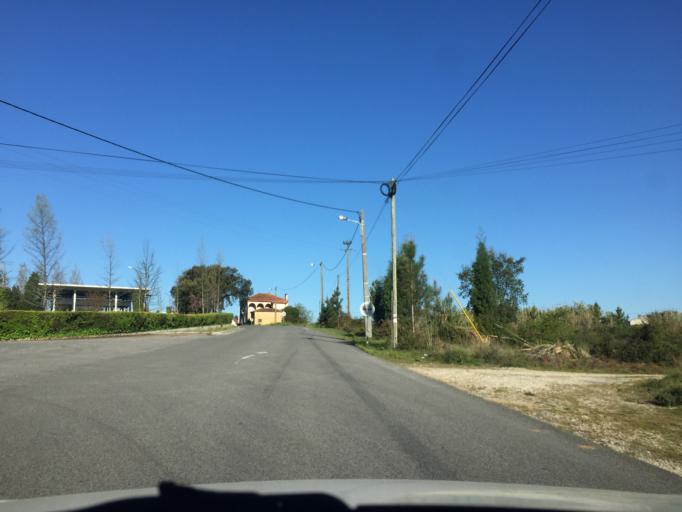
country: PT
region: Aveiro
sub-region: Anadia
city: Arcos
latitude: 40.4519
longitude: -8.4755
